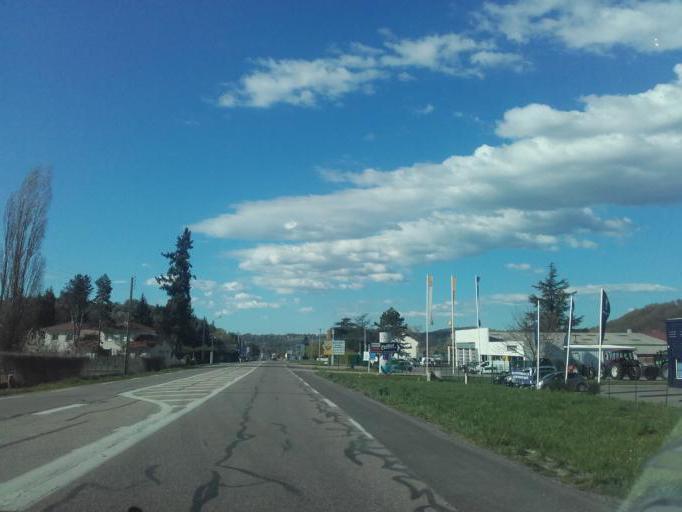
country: FR
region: Rhone-Alpes
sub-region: Departement de l'Isere
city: Nivolas-Vermelle
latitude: 45.5687
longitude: 5.3025
